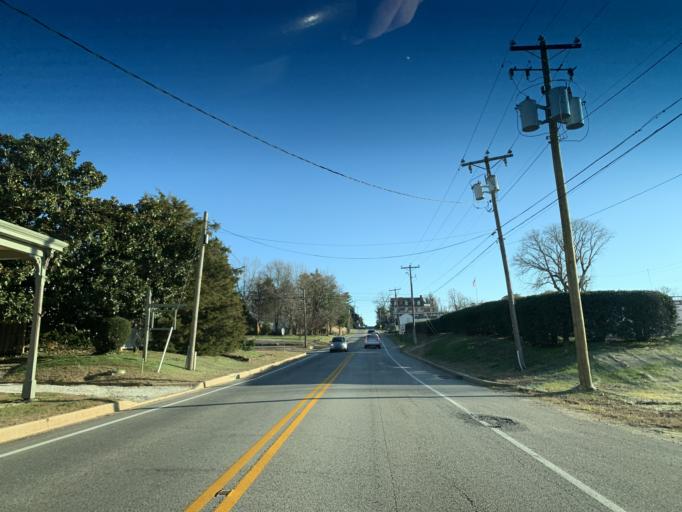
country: US
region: Delaware
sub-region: New Castle County
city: Middletown
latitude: 39.3632
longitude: -75.8813
